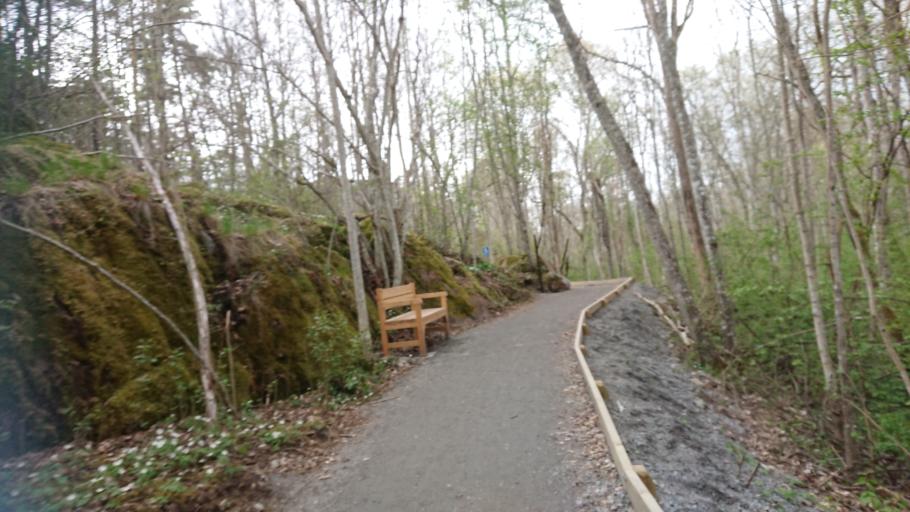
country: SE
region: Uppsala
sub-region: Uppsala Kommun
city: Uppsala
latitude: 59.8004
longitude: 17.6053
